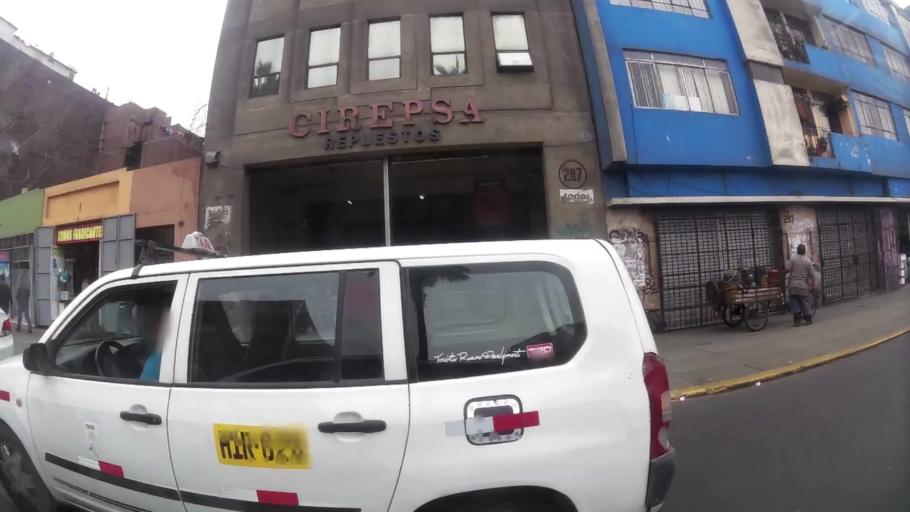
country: PE
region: Lima
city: Lima
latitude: -12.0615
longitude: -77.0295
